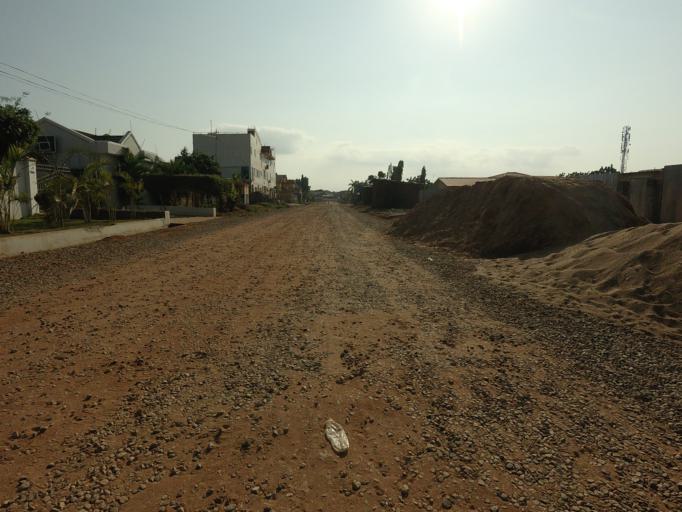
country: GH
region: Greater Accra
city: Nungua
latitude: 5.6362
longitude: -0.0889
